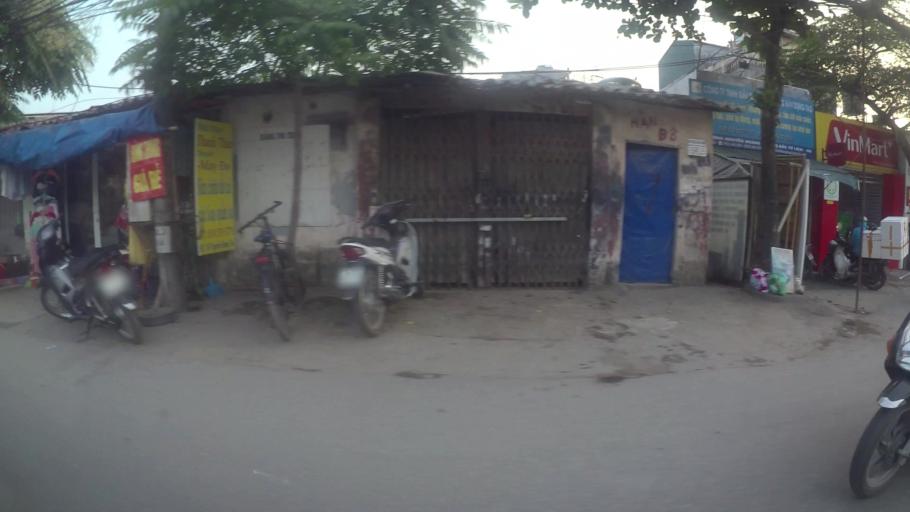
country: VN
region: Ha Noi
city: Tay Ho
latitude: 21.0729
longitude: 105.8025
